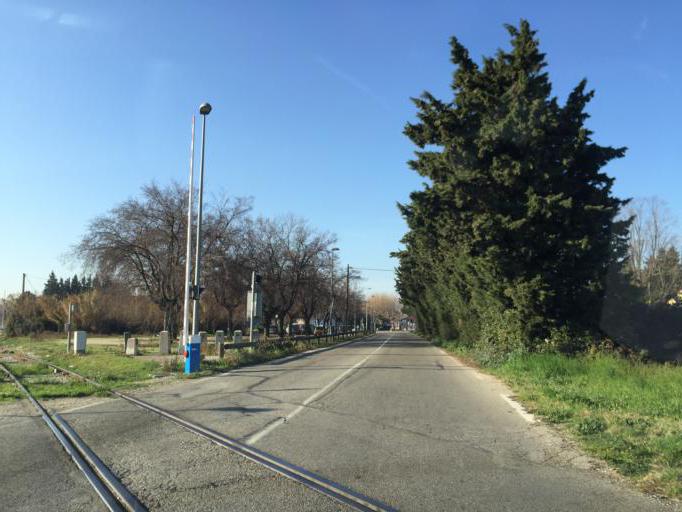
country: FR
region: Provence-Alpes-Cote d'Azur
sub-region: Departement du Vaucluse
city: Sorgues
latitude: 43.9919
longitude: 4.8660
